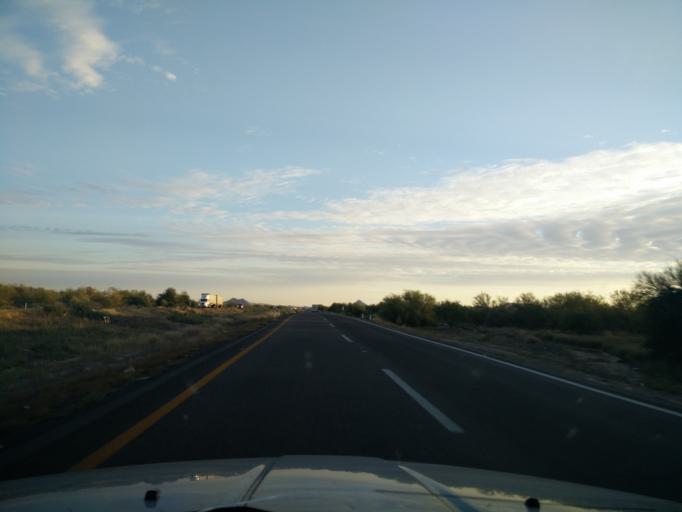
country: MX
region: Sonora
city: Hermosillo
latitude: 28.7200
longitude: -110.9815
